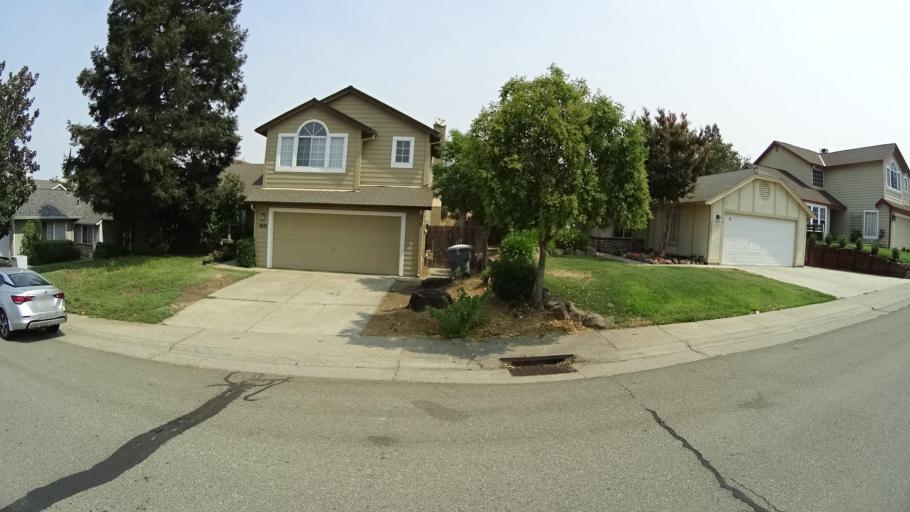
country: US
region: California
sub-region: Placer County
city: Rocklin
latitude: 38.8031
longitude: -121.2581
